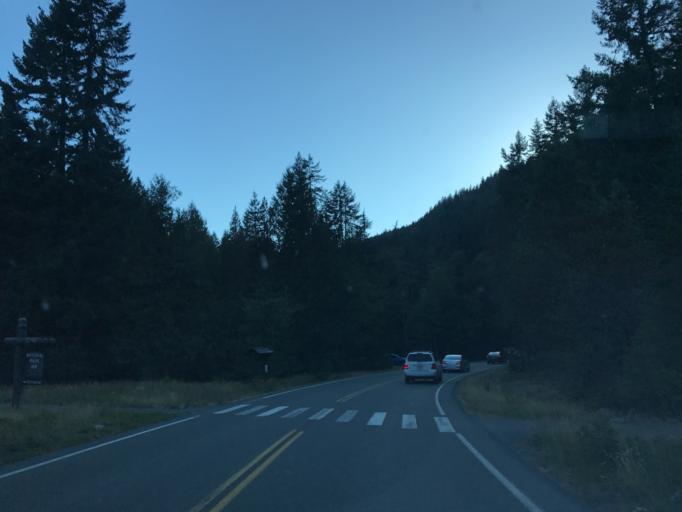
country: US
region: Washington
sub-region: Pierce County
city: Buckley
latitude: 46.7497
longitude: -121.8136
